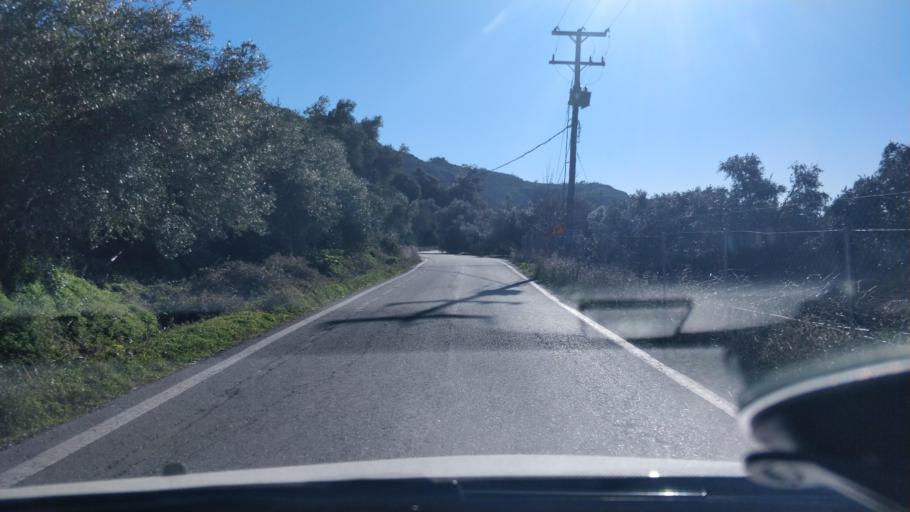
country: GR
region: Crete
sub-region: Nomos Lasithiou
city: Kritsa
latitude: 35.0792
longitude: 25.5967
